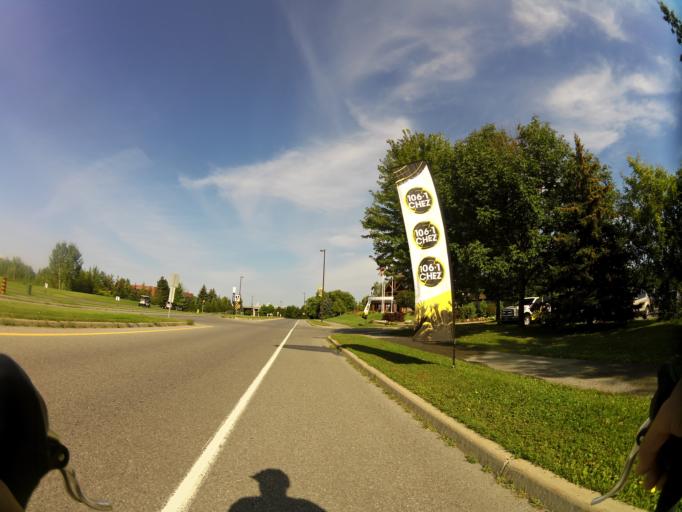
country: CA
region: Ontario
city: Bells Corners
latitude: 45.3518
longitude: -75.9115
